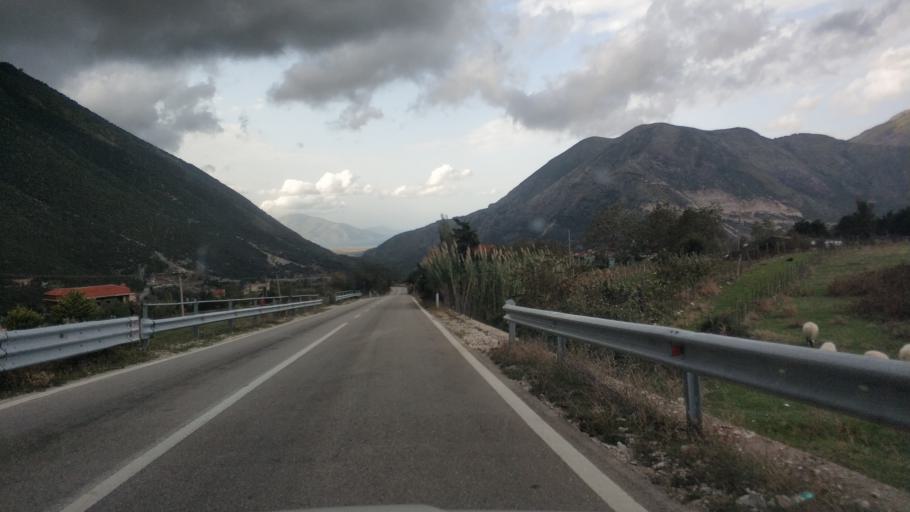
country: AL
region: Vlore
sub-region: Rrethi i Vlores
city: Brataj
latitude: 40.2326
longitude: 19.5626
